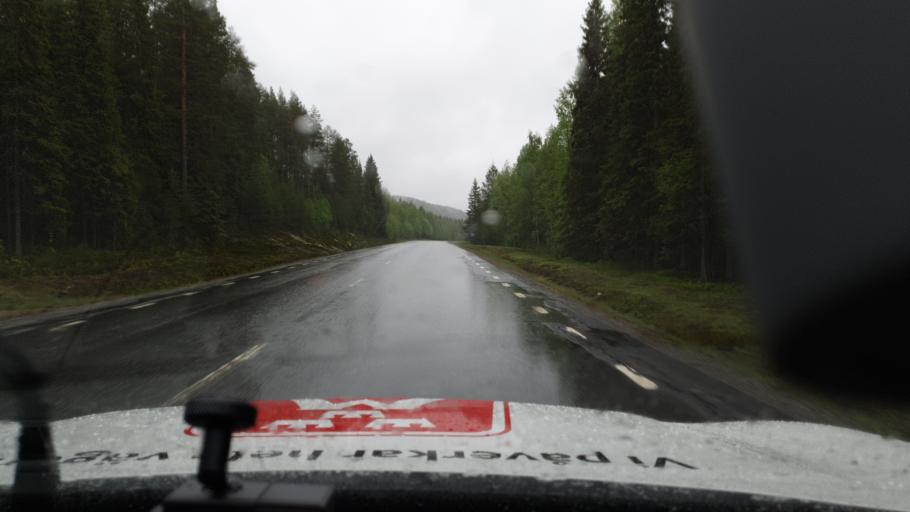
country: SE
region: Vaesterbotten
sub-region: Vannas Kommun
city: Vannasby
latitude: 64.0791
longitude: 19.9839
